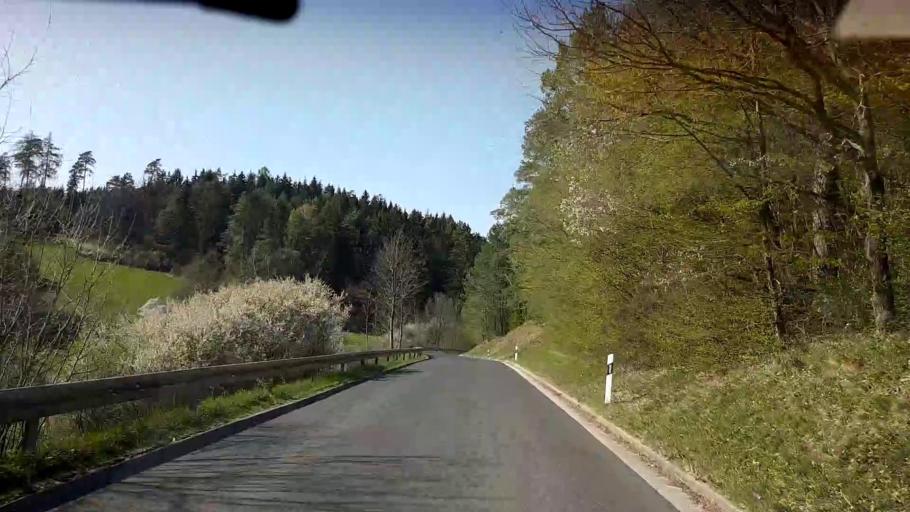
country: DE
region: Bavaria
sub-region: Upper Franconia
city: Waischenfeld
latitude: 49.8274
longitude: 11.3520
